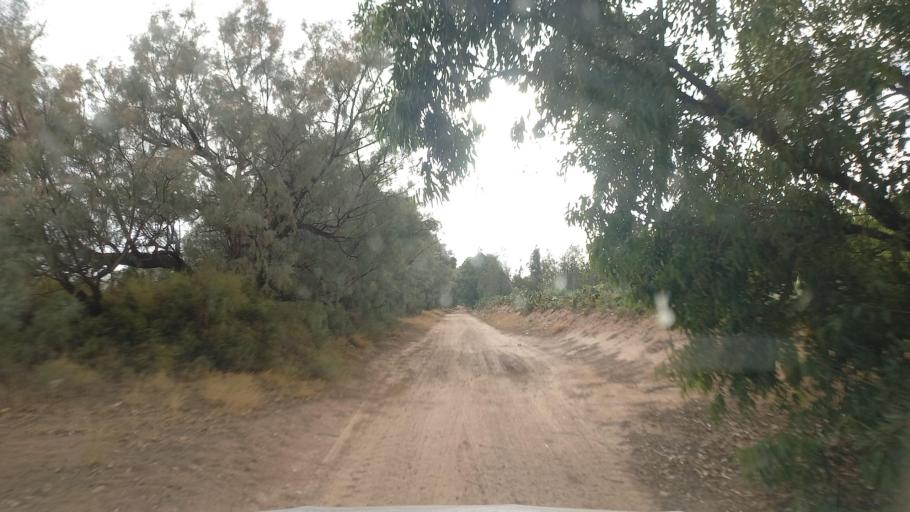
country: TN
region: Al Qasrayn
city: Sbiba
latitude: 35.2944
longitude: 9.0658
